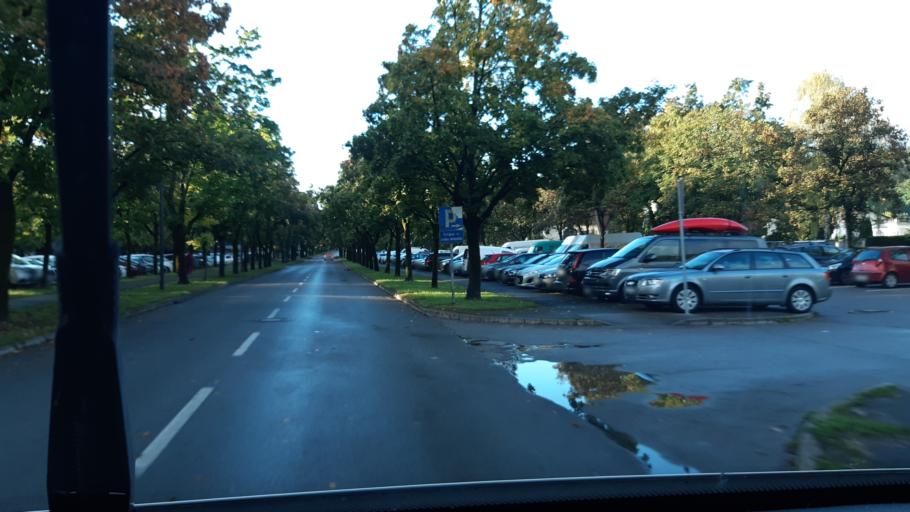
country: SI
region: Ljubljana
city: Ljubljana
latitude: 46.0532
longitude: 14.5430
